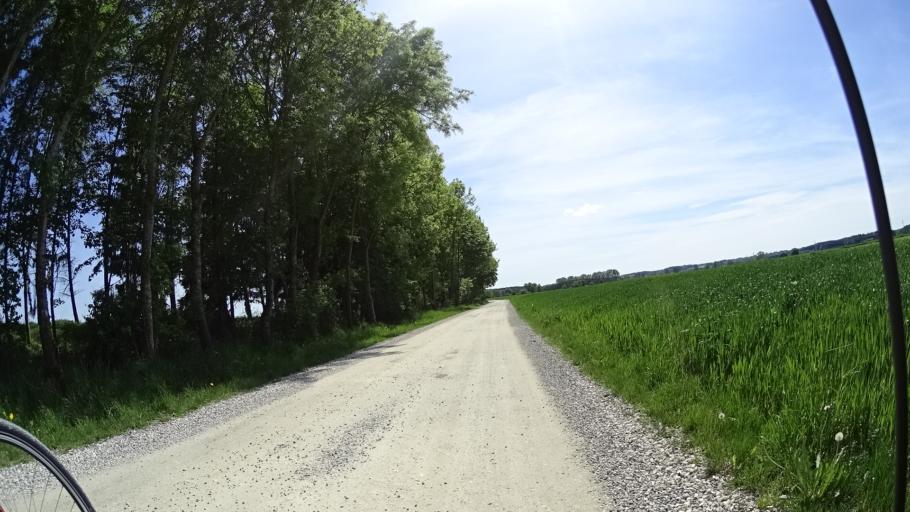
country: DE
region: Bavaria
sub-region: Swabia
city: Weissenhorn
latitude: 48.3238
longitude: 10.1504
